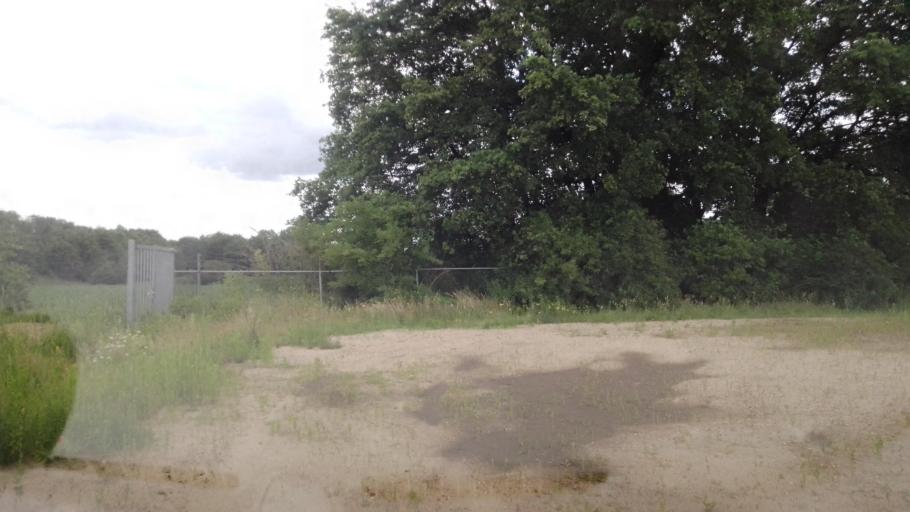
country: NL
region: Limburg
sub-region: Gemeente Venlo
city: Venlo
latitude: 51.3941
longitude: 6.1476
